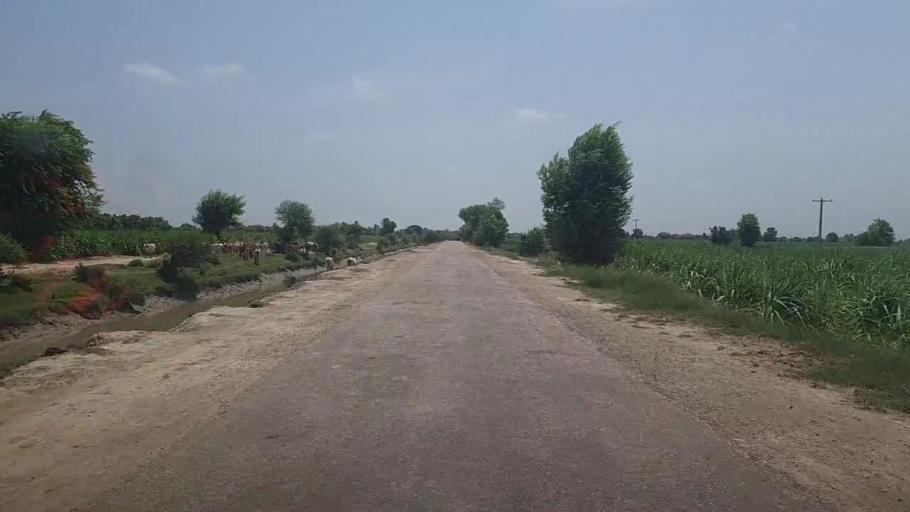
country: PK
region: Sindh
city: Ubauro
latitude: 28.2932
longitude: 69.8060
